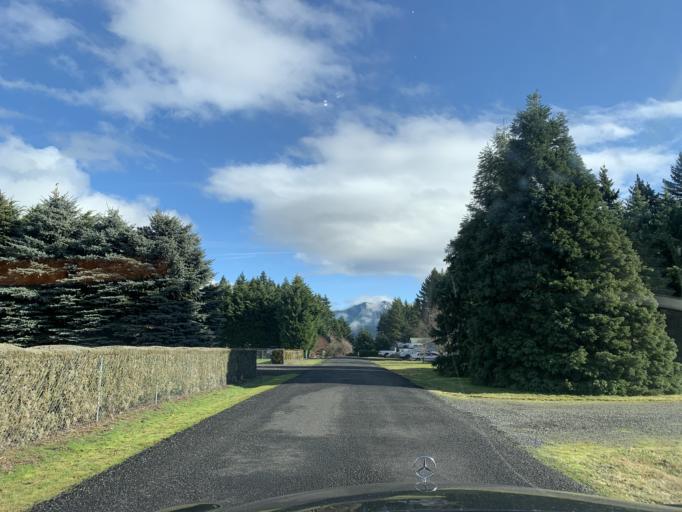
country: US
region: Washington
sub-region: Skamania County
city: Carson
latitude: 45.7237
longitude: -121.8149
